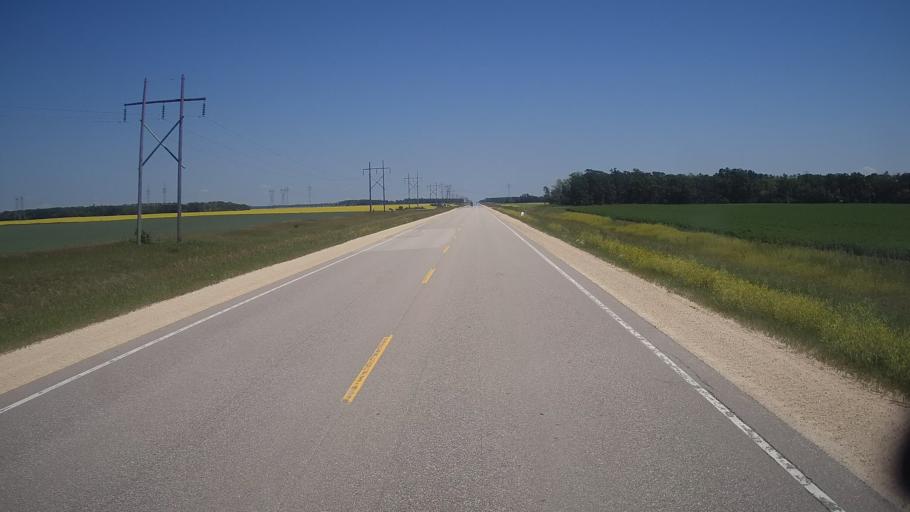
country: CA
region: Manitoba
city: Stonewall
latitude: 50.1227
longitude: -97.5098
